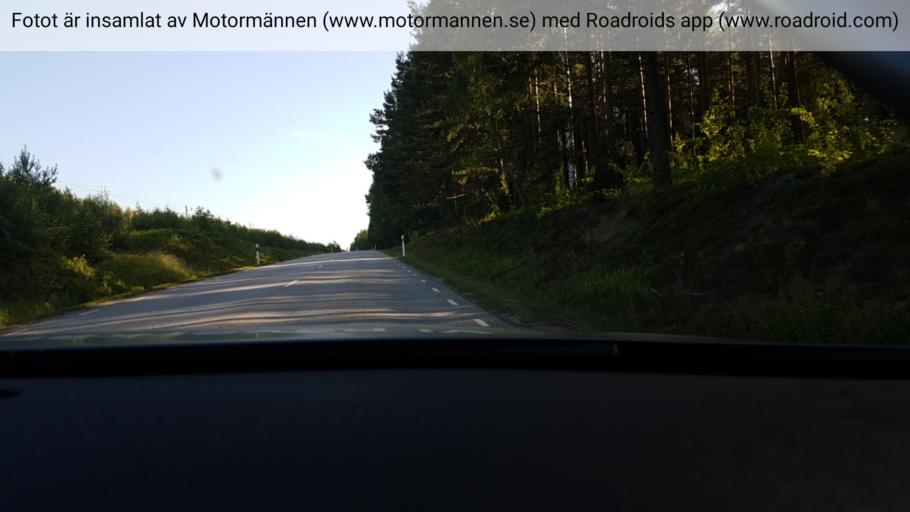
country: SE
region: Vaestra Goetaland
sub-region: Toreboda Kommun
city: Toereboda
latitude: 58.6675
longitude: 14.0930
